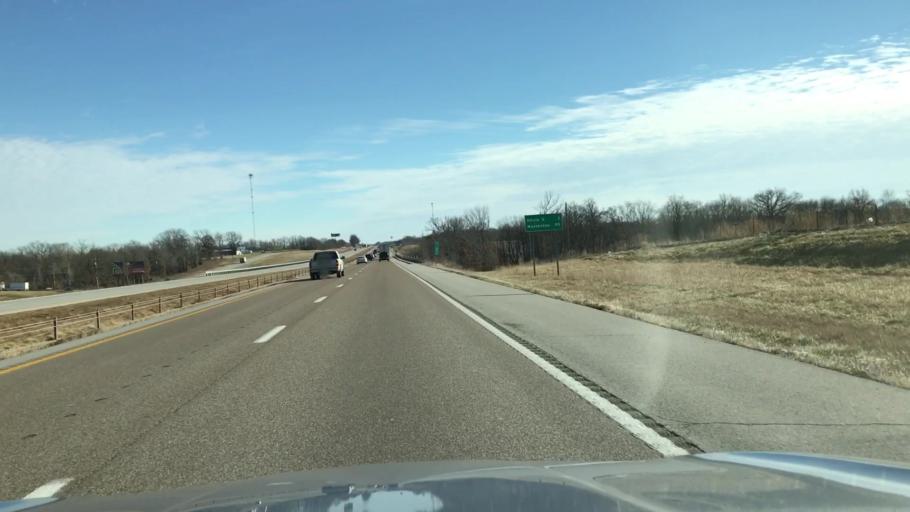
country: US
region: Missouri
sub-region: Cooper County
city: Boonville
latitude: 38.9348
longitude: -92.8350
